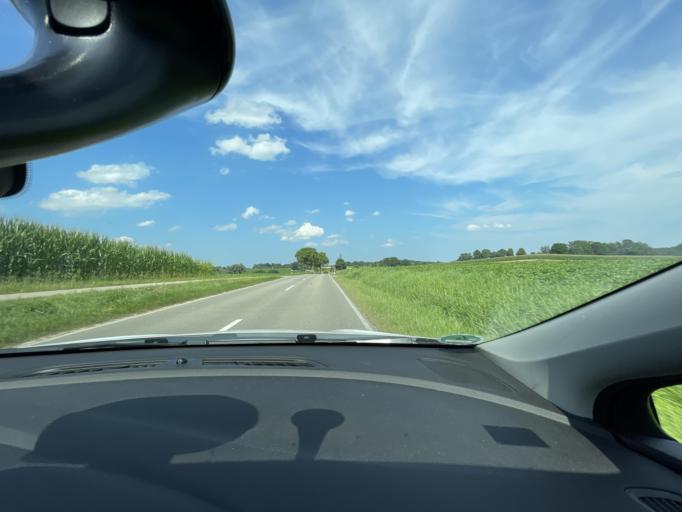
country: DE
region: Bavaria
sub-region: Upper Bavaria
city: Altomunster
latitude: 48.4154
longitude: 11.3001
